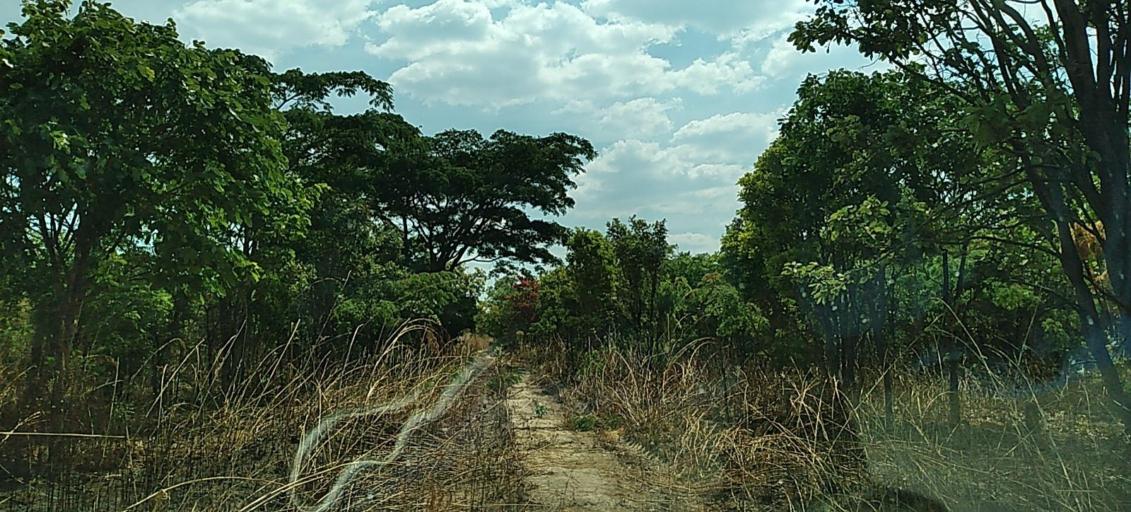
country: ZM
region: Copperbelt
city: Chililabombwe
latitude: -12.3314
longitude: 27.7648
